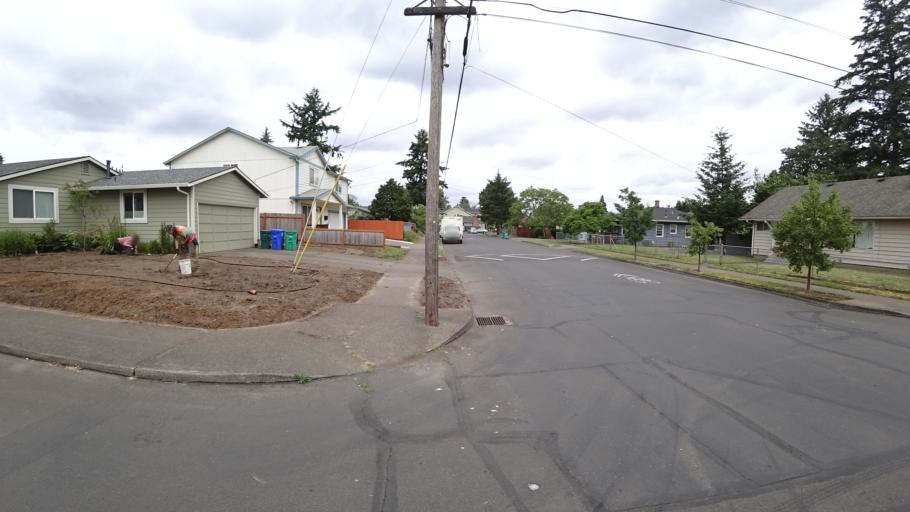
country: US
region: Oregon
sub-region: Multnomah County
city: Lents
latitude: 45.4749
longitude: -122.5739
